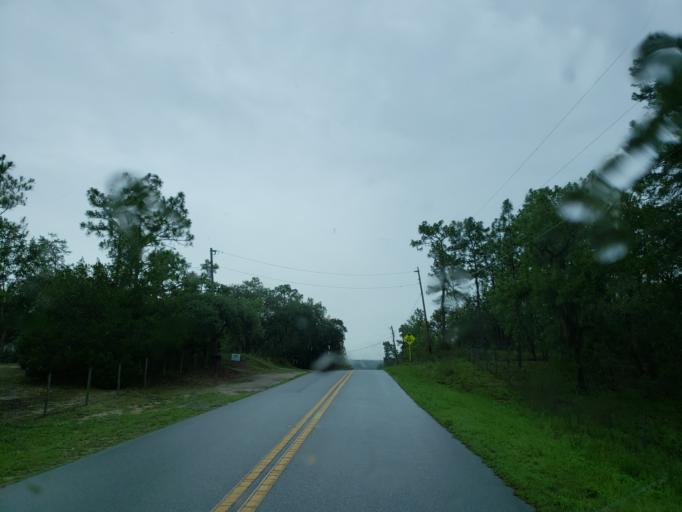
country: US
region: Florida
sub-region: Citrus County
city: Floral City
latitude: 28.6687
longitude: -82.3186
